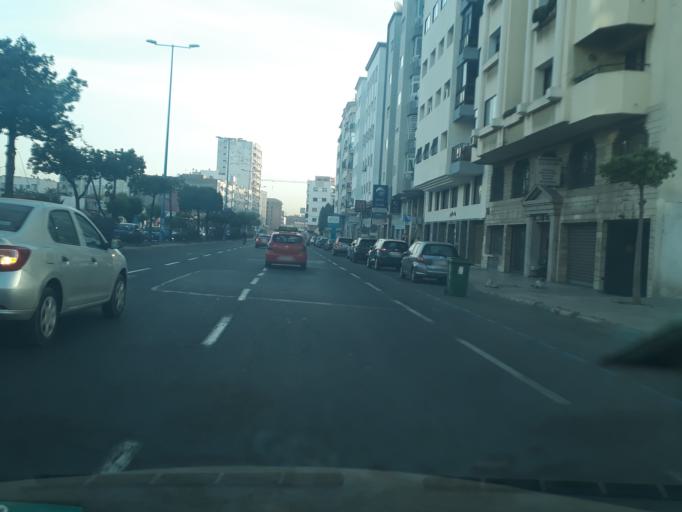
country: MA
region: Grand Casablanca
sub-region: Casablanca
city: Casablanca
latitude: 33.5745
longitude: -7.6399
